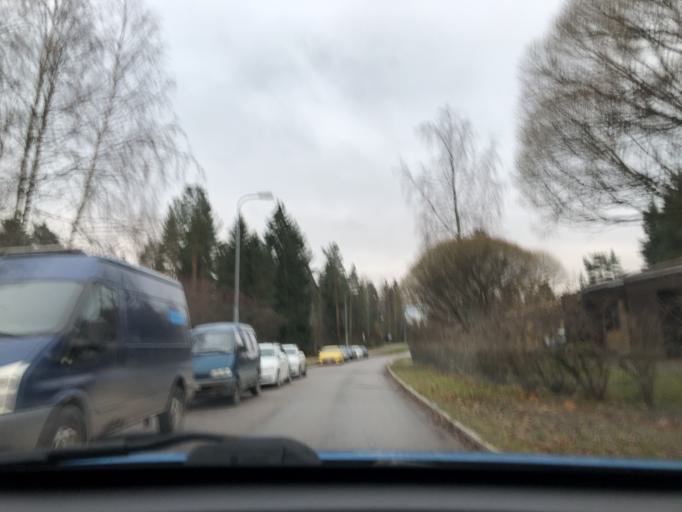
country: FI
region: Pirkanmaa
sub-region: Tampere
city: Kangasala
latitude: 61.5263
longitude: 23.9519
